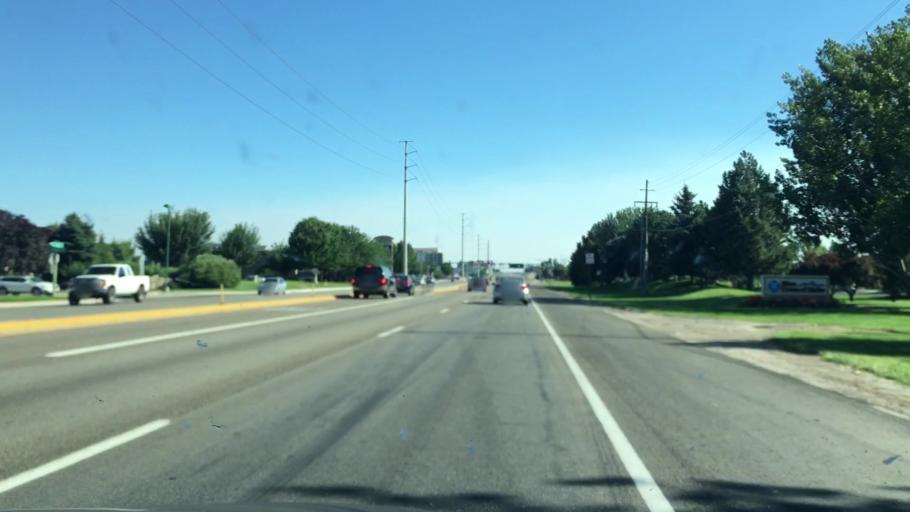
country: US
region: Idaho
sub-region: Ada County
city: Meridian
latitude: 43.6151
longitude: -116.3547
